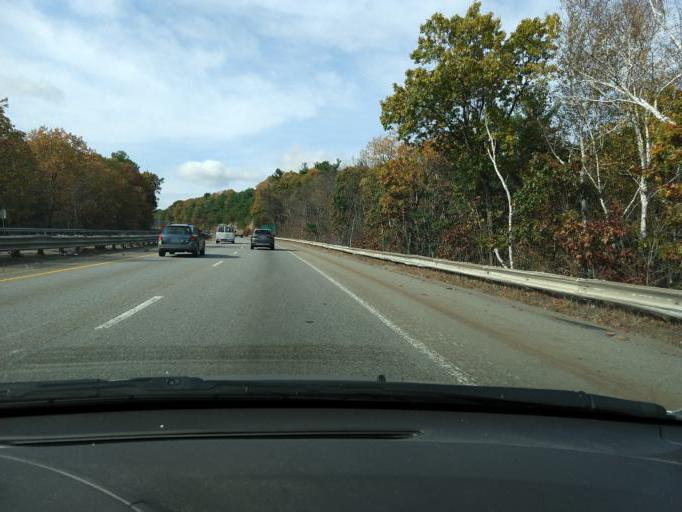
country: US
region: Massachusetts
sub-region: Middlesex County
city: Littleton Common
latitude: 42.5285
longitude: -71.5270
